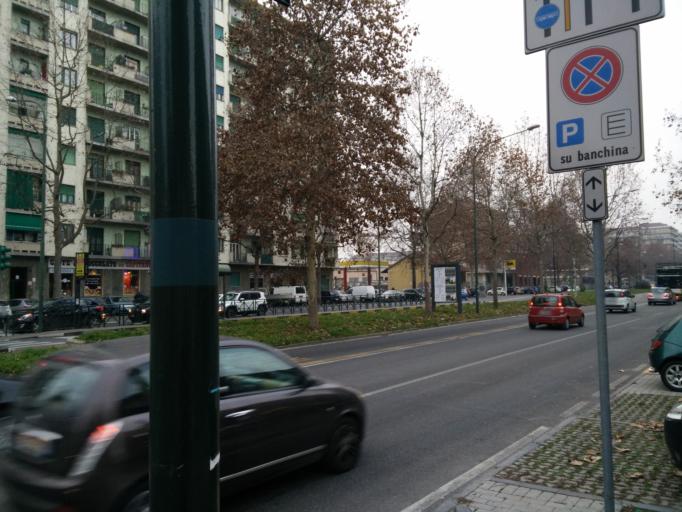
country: IT
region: Piedmont
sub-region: Provincia di Torino
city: Nichelino
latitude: 45.0207
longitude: 7.6547
